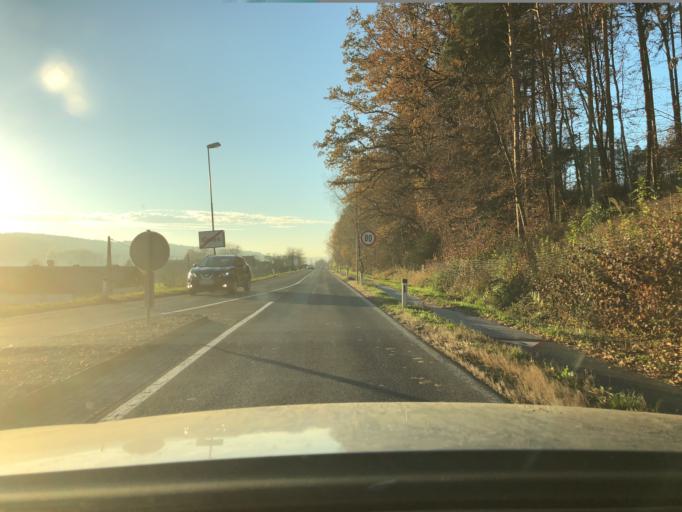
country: AT
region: Styria
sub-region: Politischer Bezirk Weiz
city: Sinabelkirchen
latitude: 47.0994
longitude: 15.8415
